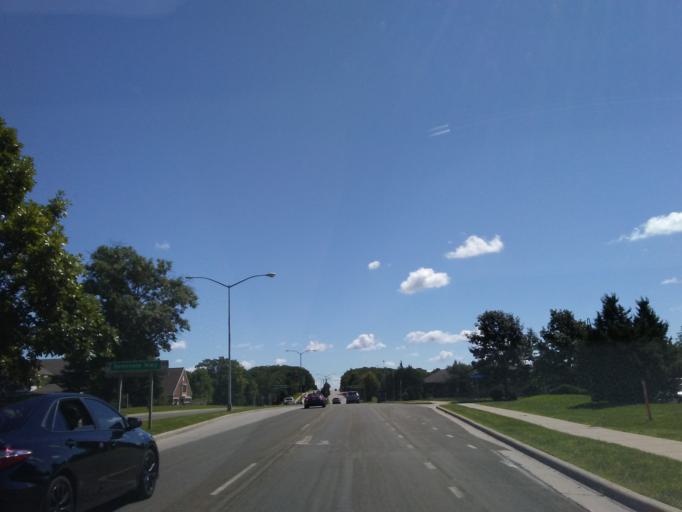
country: US
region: Wisconsin
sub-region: Dane County
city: Fitchburg
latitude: 43.0153
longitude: -89.4580
